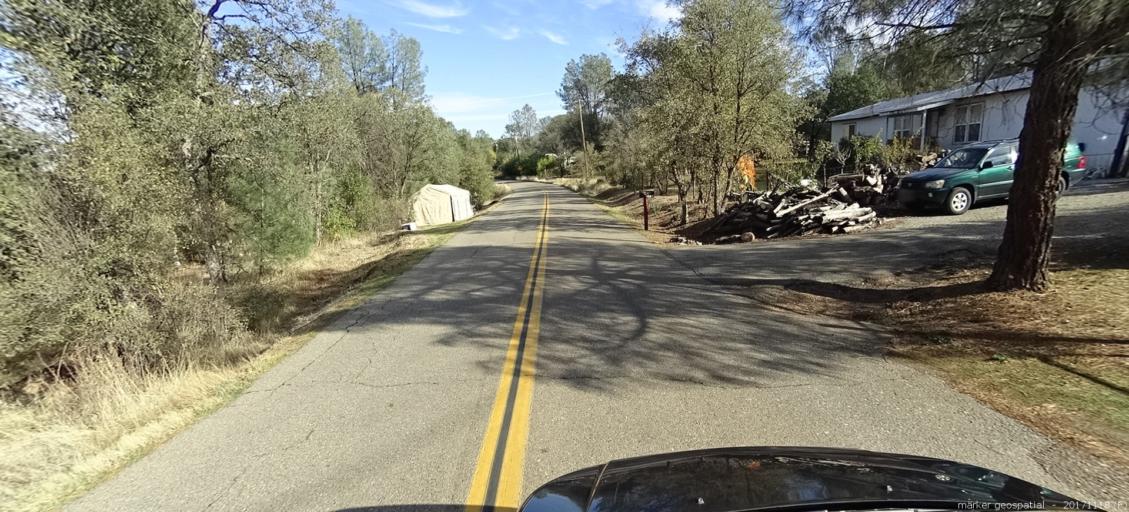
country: US
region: California
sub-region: Shasta County
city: Redding
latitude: 40.4720
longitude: -122.4178
